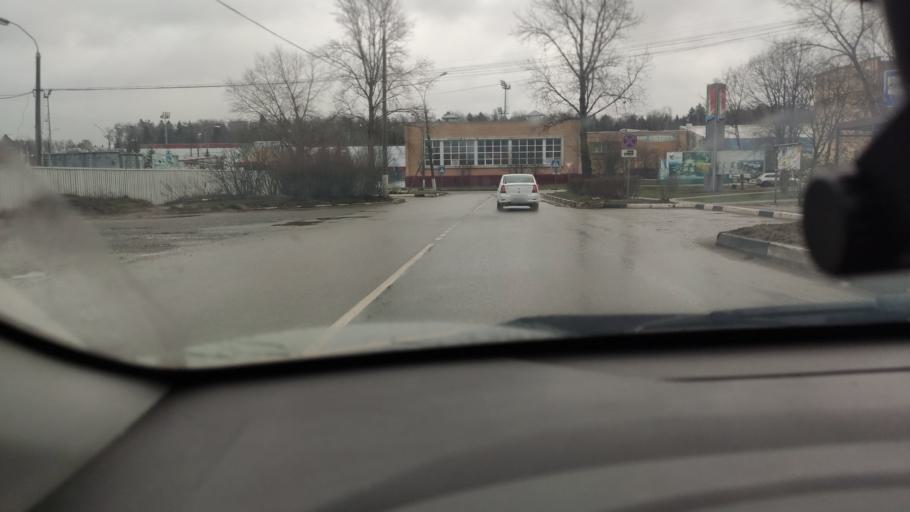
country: RU
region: Moskovskaya
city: Selyatino
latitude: 55.5183
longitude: 36.9815
